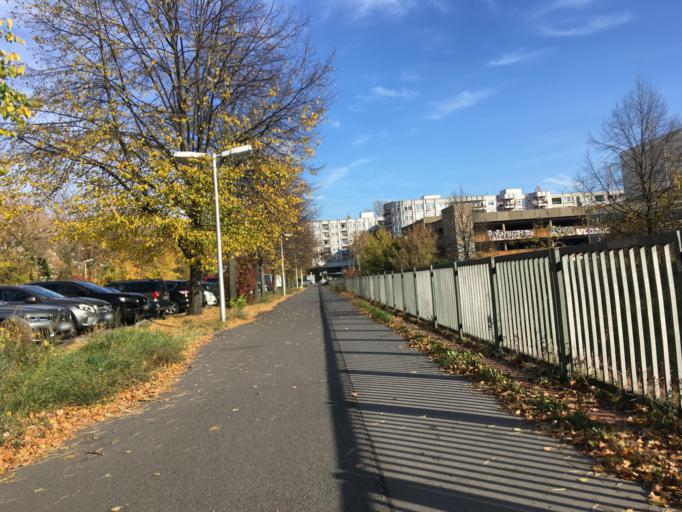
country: DE
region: Berlin
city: Wedding Bezirk
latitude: 52.5382
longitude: 13.3701
